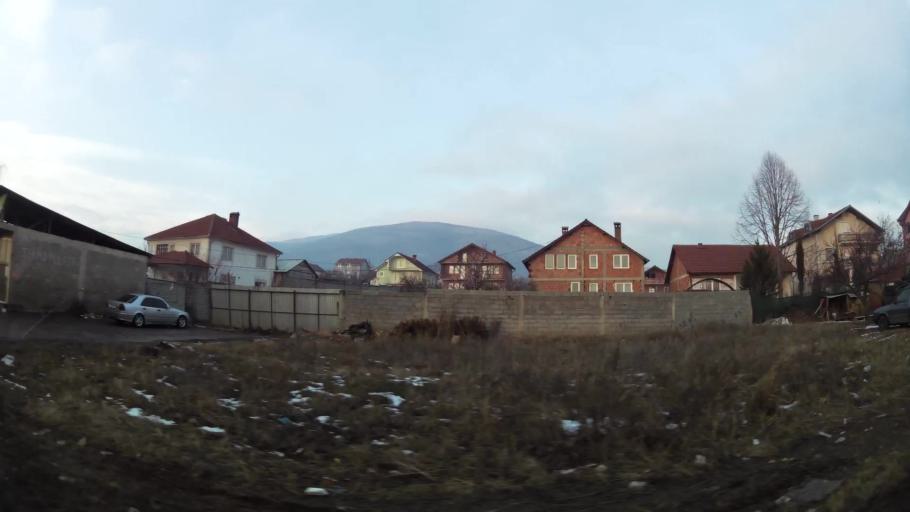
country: MK
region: Aracinovo
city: Arachinovo
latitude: 42.0271
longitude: 21.5666
